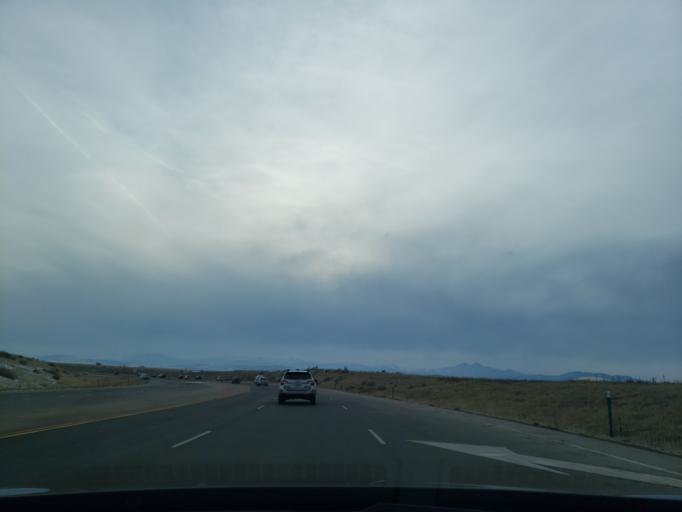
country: US
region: Colorado
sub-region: Larimer County
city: Campion
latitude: 40.3355
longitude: -105.0973
